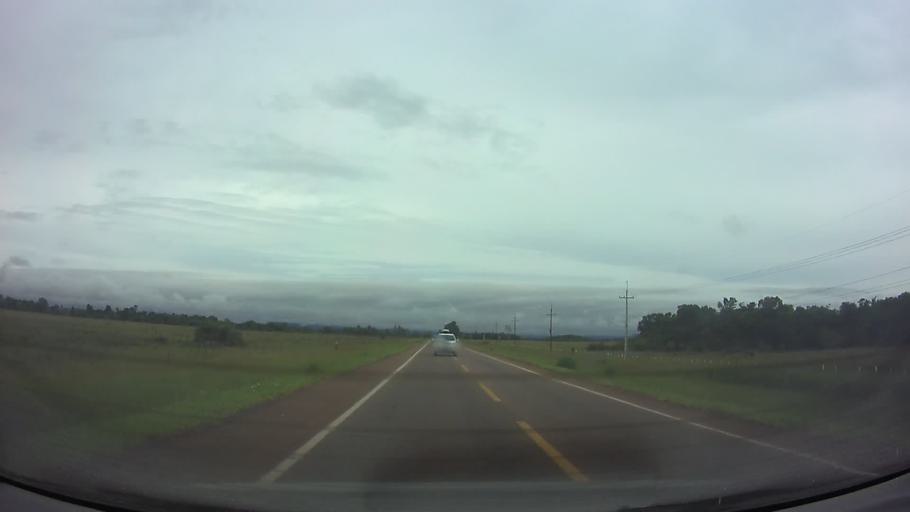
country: PY
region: Paraguari
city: Carapegua
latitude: -25.7180
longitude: -57.1978
